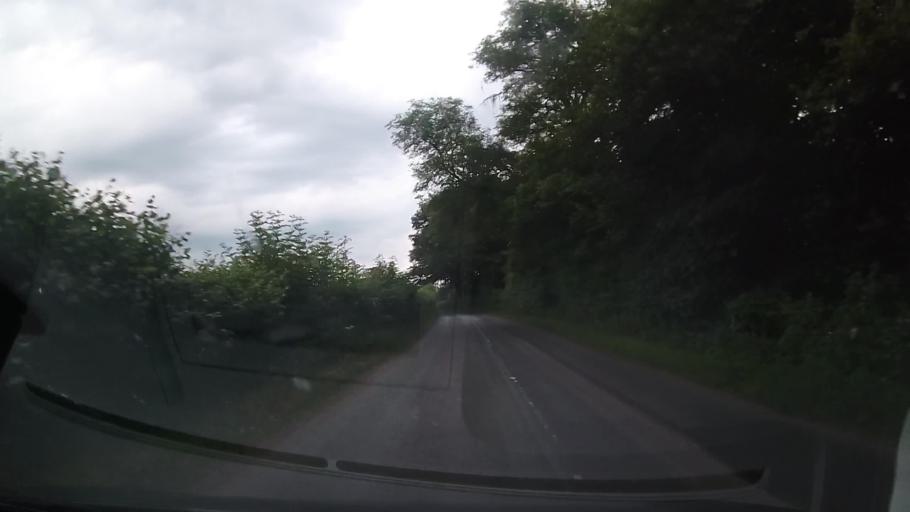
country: GB
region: Wales
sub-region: Sir Powys
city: Llanrhaeadr-ym-Mochnant
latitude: 52.8141
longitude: -3.2963
